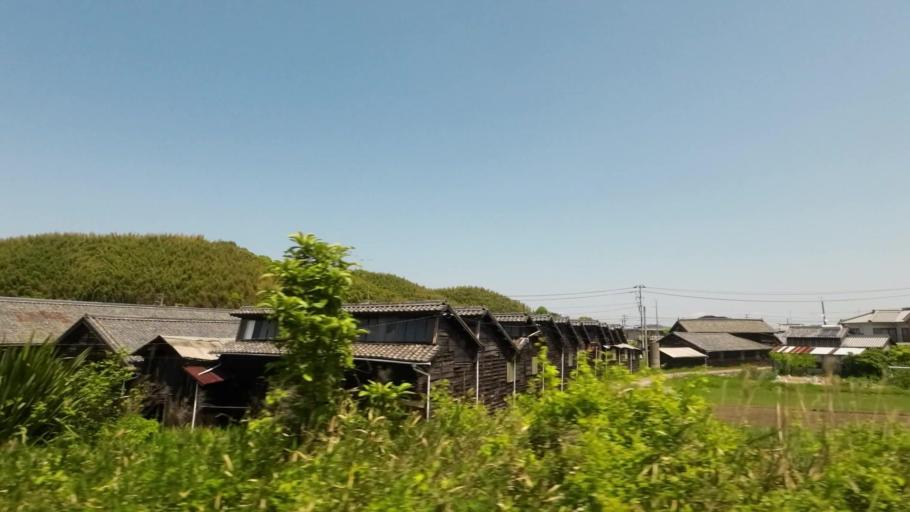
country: JP
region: Ehime
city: Hojo
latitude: 34.0623
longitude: 132.8998
